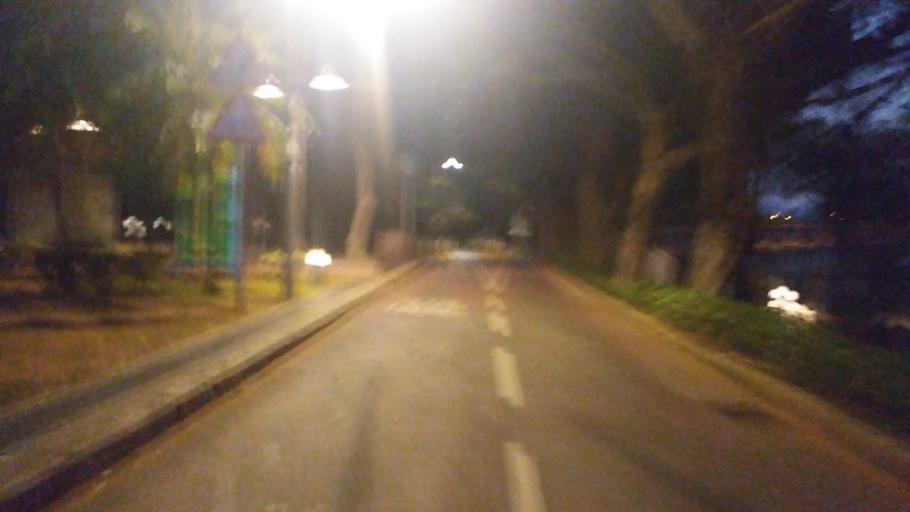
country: HK
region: Yuen Long
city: Yuen Long Kau Hui
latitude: 22.4524
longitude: 113.9984
